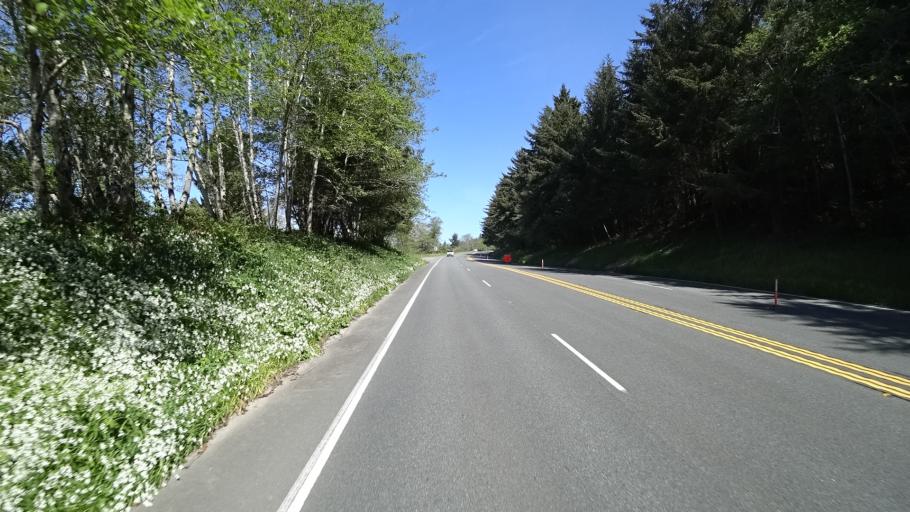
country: US
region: California
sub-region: Del Norte County
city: Bertsch-Oceanview
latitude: 41.6096
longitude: -124.1045
